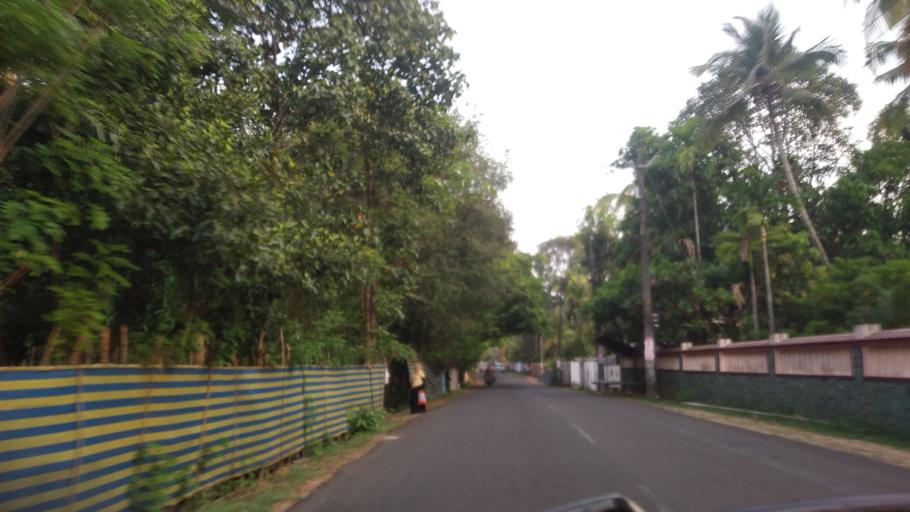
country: IN
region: Kerala
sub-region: Thrissur District
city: Thanniyam
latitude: 10.3388
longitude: 76.1178
